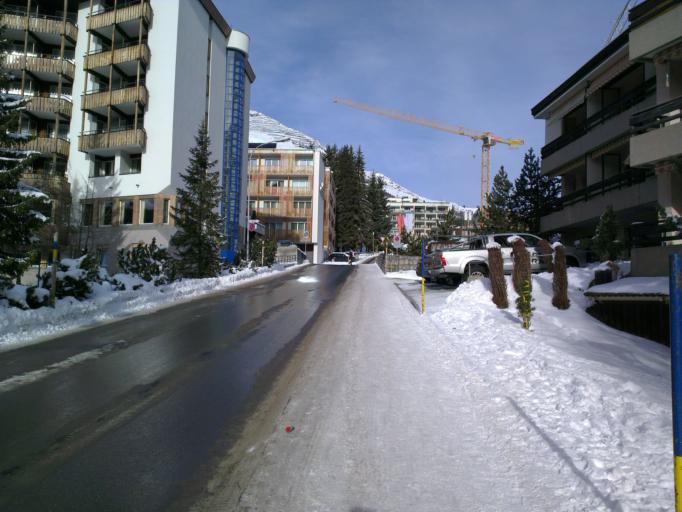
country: CH
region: Grisons
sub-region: Praettigau/Davos District
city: Davos
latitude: 46.8008
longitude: 9.8324
